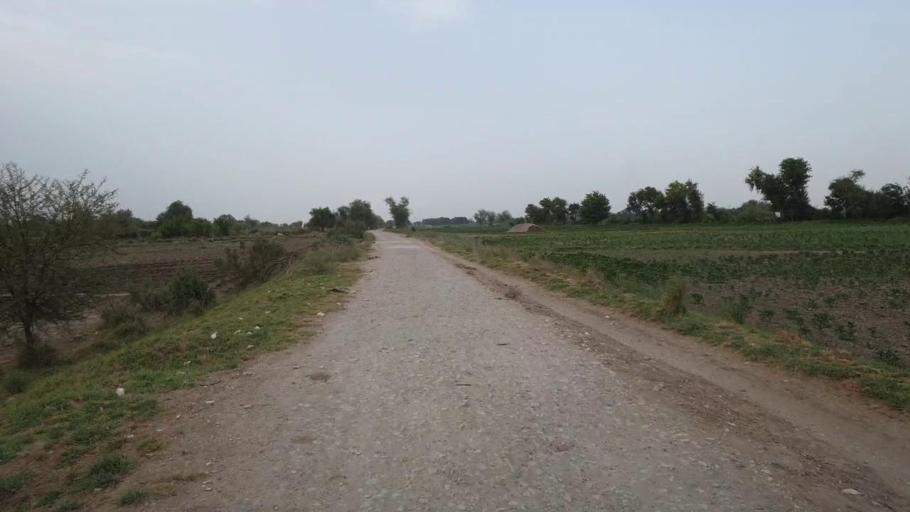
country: PK
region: Sindh
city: Bandhi
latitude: 26.5182
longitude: 68.1805
